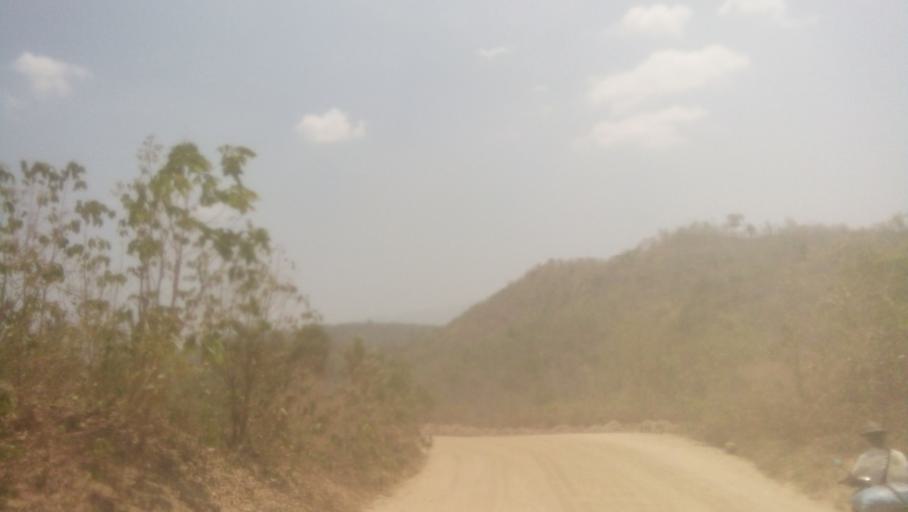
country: TH
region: Tak
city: Tha Song Yang
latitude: 17.2947
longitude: 97.8350
